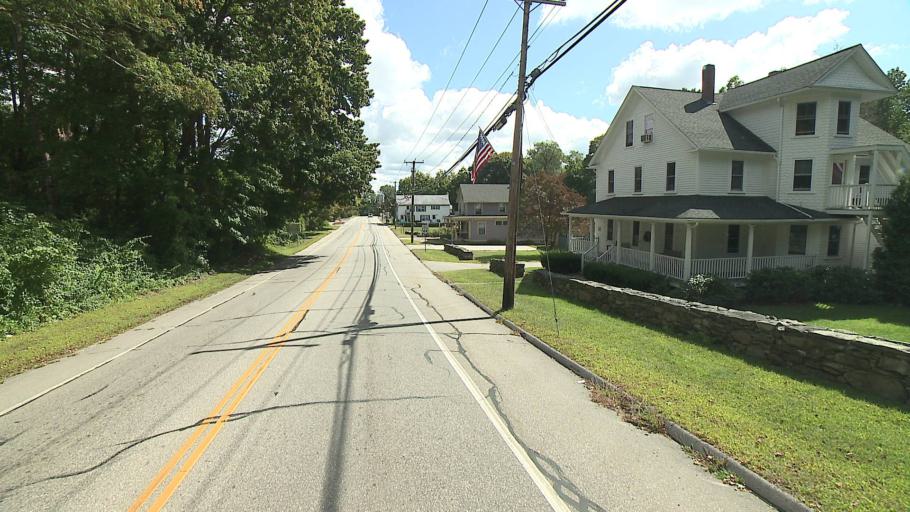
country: US
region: Connecticut
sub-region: Windham County
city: South Woodstock
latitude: 41.8976
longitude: -71.9617
